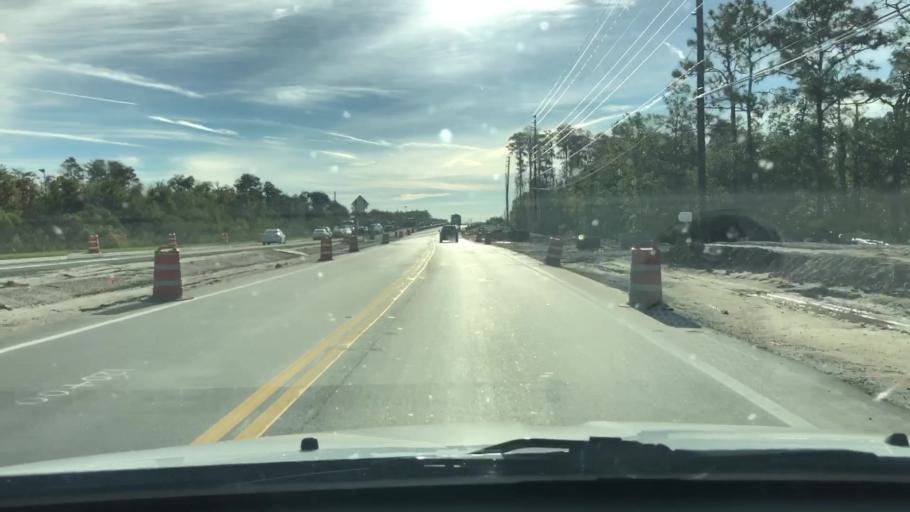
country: US
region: Florida
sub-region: Orange County
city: Meadow Woods
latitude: 28.3931
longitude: -81.3242
